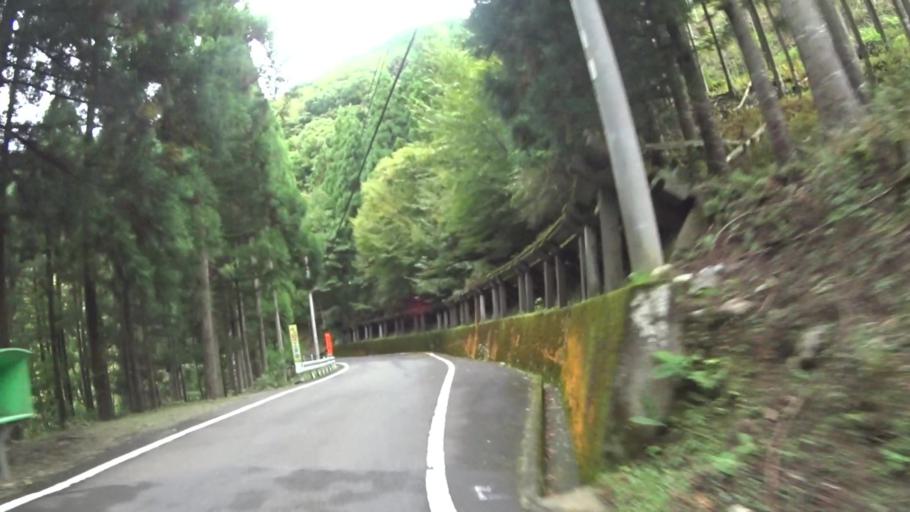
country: JP
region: Fukui
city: Obama
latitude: 35.3174
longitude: 135.6891
